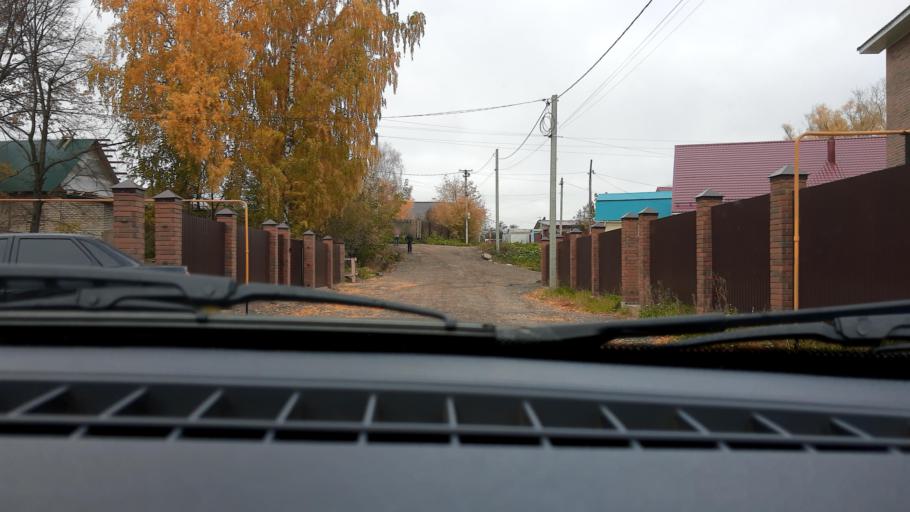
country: RU
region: Bashkortostan
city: Mikhaylovka
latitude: 54.7945
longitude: 55.8901
